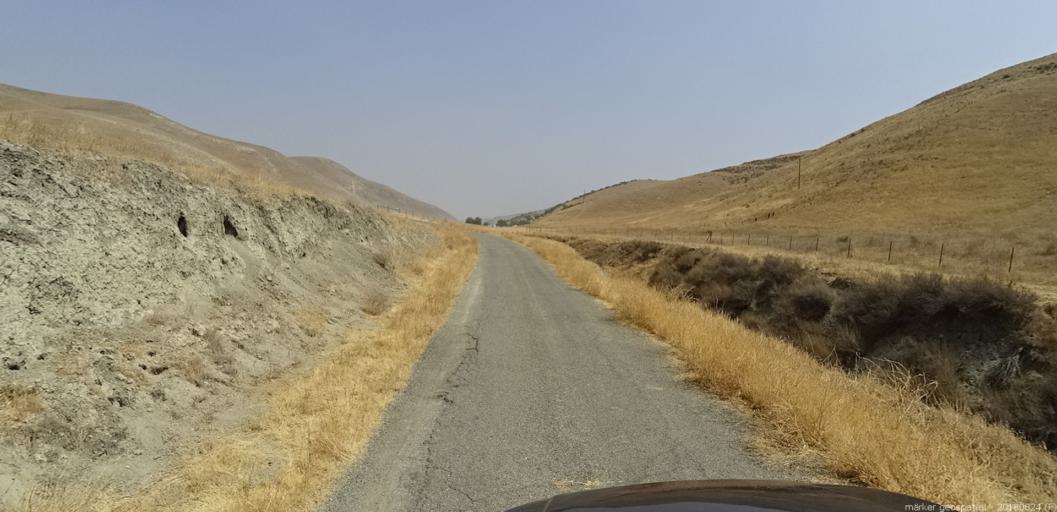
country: US
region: California
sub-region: Monterey County
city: King City
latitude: 36.1971
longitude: -120.9495
